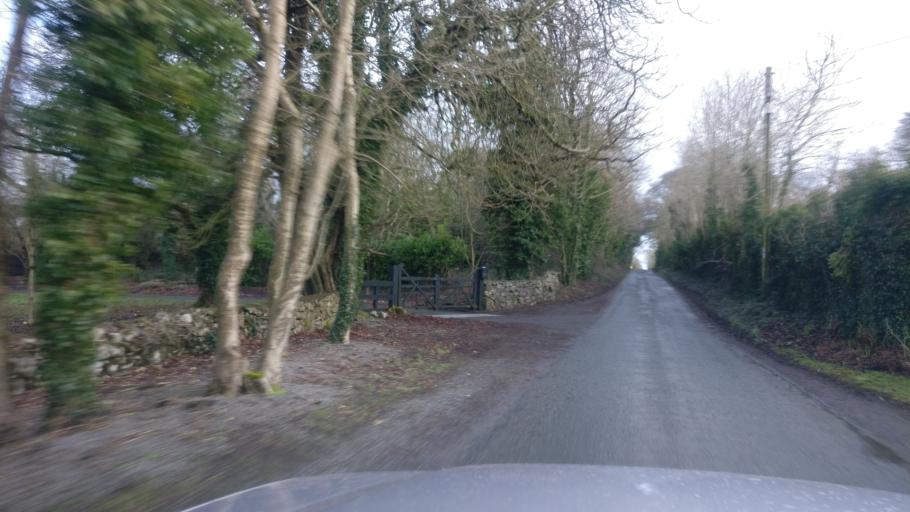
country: IE
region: Connaught
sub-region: County Galway
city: Athenry
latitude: 53.2623
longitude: -8.7027
